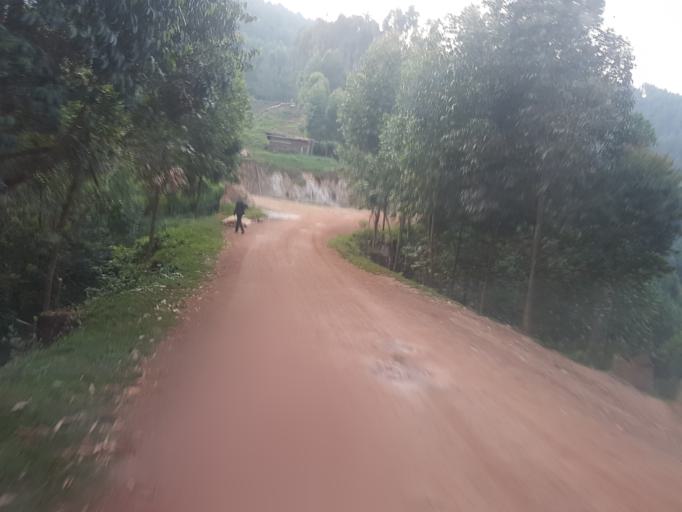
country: UG
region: Western Region
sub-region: Kanungu District
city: Kanungu
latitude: -1.0015
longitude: 29.8471
